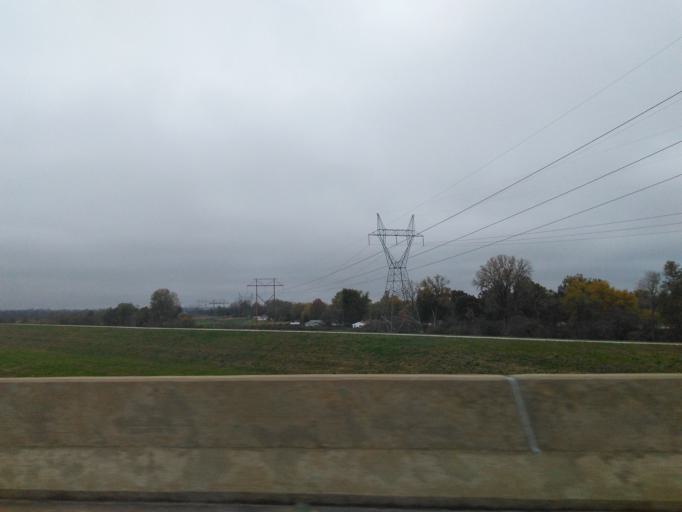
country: US
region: Illinois
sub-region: Saint Clair County
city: Cahokia
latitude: 38.5476
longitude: -90.1672
